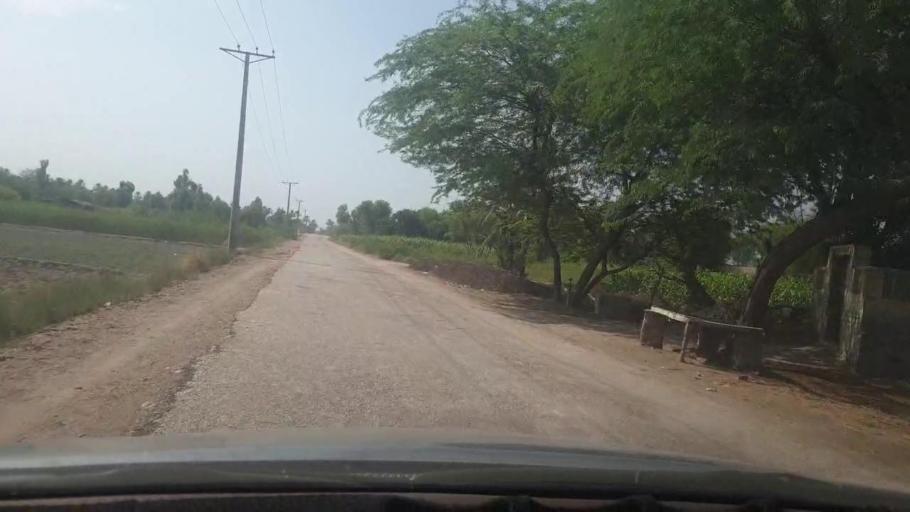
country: PK
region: Sindh
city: Gambat
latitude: 27.3298
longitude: 68.5498
